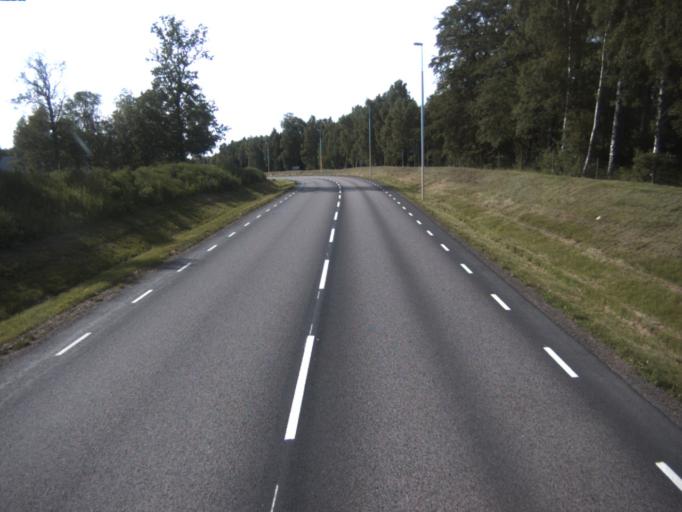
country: SE
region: Skane
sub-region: Helsingborg
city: Odakra
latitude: 56.0940
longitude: 12.7681
